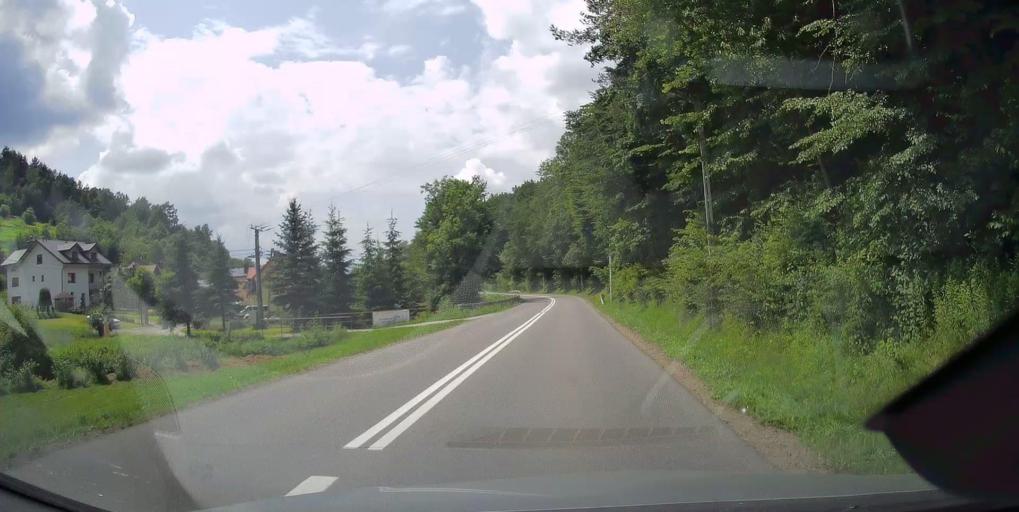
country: PL
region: Lesser Poland Voivodeship
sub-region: Powiat nowosadecki
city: Nowy Sacz
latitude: 49.6475
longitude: 20.7201
